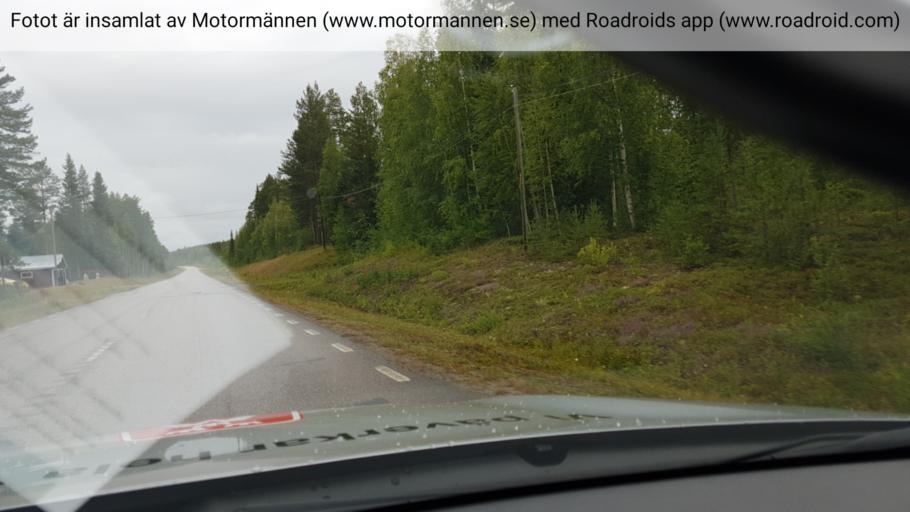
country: SE
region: Norrbotten
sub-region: Alvsbyns Kommun
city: AElvsbyn
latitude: 66.1134
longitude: 20.9284
